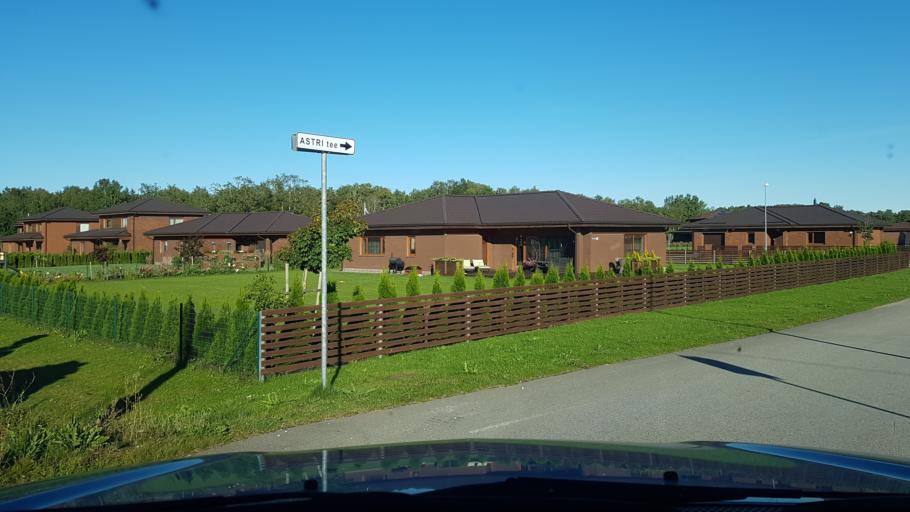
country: EE
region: Harju
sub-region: Rae vald
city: Jueri
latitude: 59.3898
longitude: 24.8545
